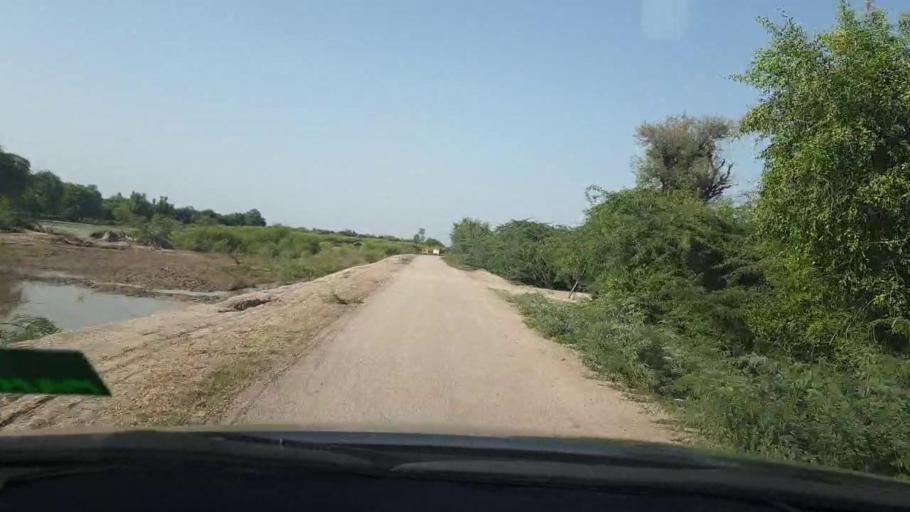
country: PK
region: Sindh
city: Naukot
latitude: 24.8707
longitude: 69.3171
